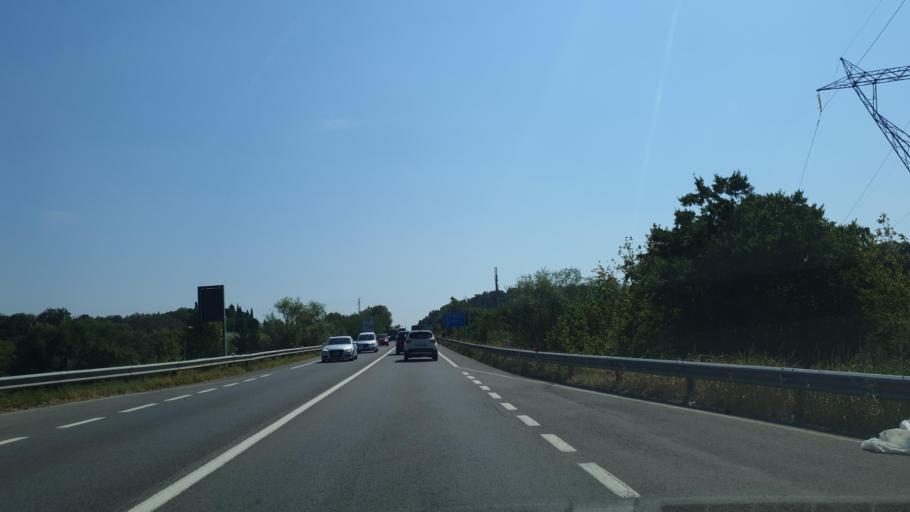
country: IT
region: Lombardy
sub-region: Provincia di Brescia
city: Lonato
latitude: 45.4656
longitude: 10.5023
